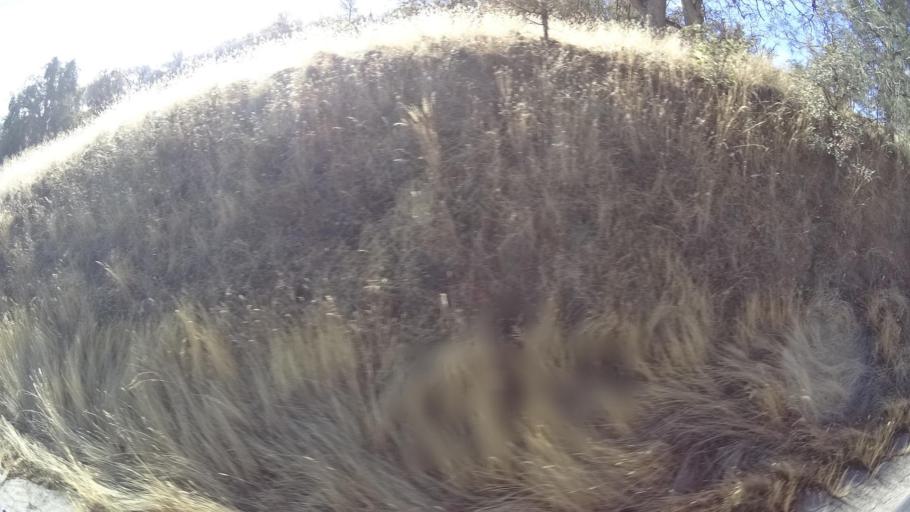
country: US
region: California
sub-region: Kern County
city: Alta Sierra
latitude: 35.6314
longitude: -118.7747
